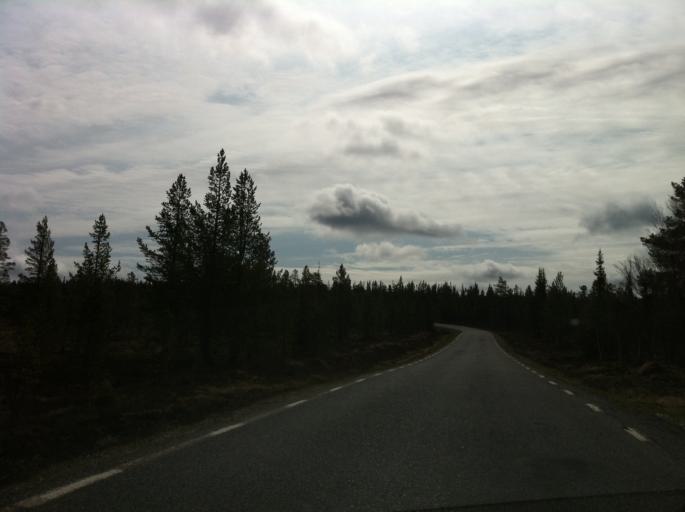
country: NO
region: Hedmark
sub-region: Engerdal
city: Engerdal
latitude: 62.3150
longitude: 12.8087
